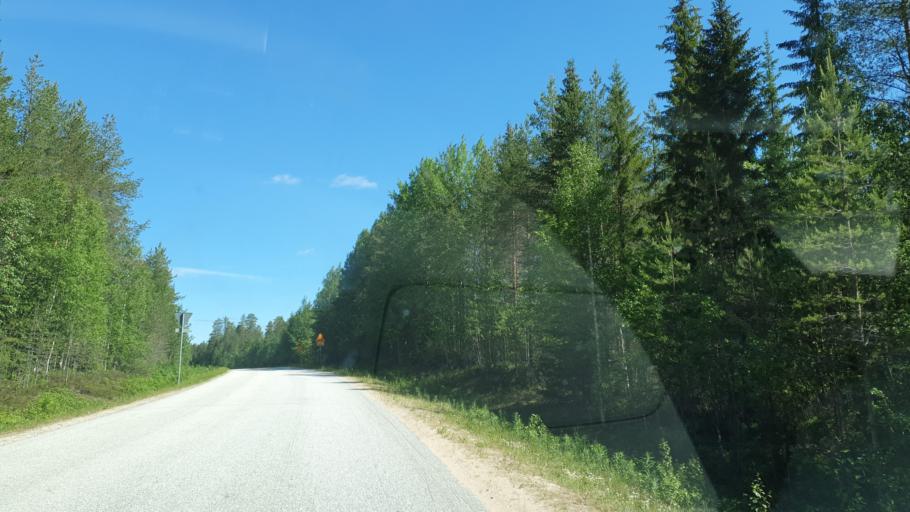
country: FI
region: Kainuu
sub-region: Kehys-Kainuu
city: Kuhmo
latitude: 64.4599
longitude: 29.5332
